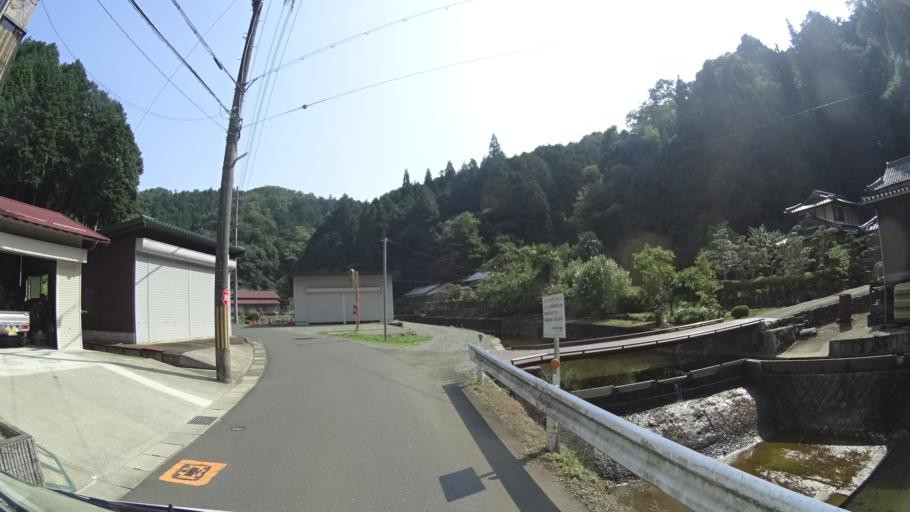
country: JP
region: Kyoto
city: Maizuru
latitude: 35.4217
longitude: 135.2222
